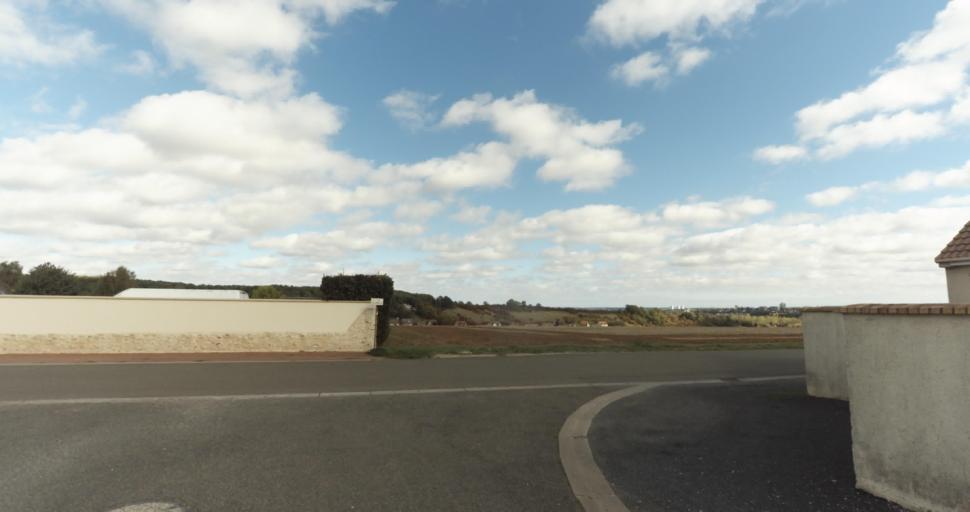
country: FR
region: Centre
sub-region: Departement d'Eure-et-Loir
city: Garnay
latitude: 48.7164
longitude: 1.3378
